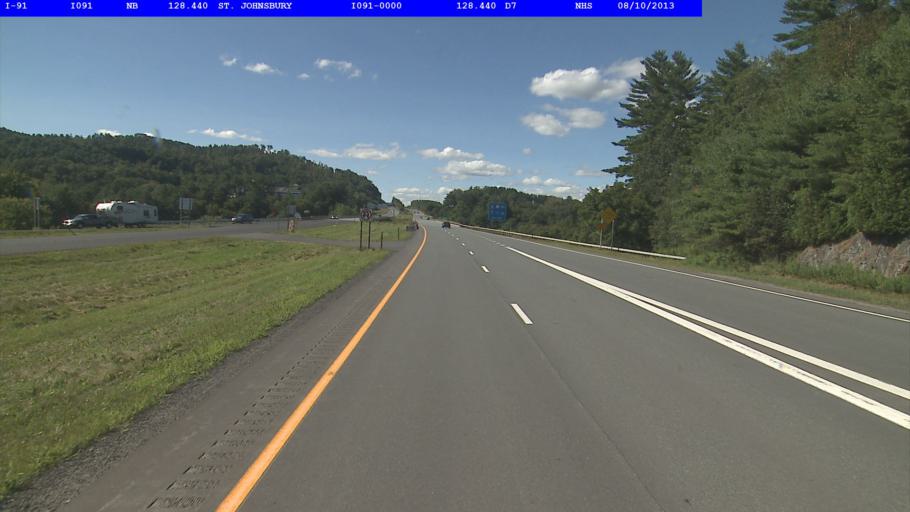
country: US
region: Vermont
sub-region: Caledonia County
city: Saint Johnsbury
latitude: 44.3990
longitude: -72.0187
